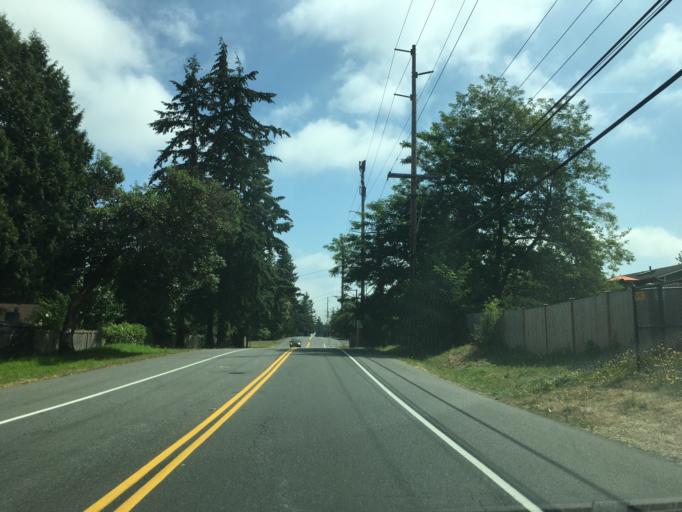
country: US
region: Washington
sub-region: King County
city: Inglewood-Finn Hill
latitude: 47.7188
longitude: -122.2292
